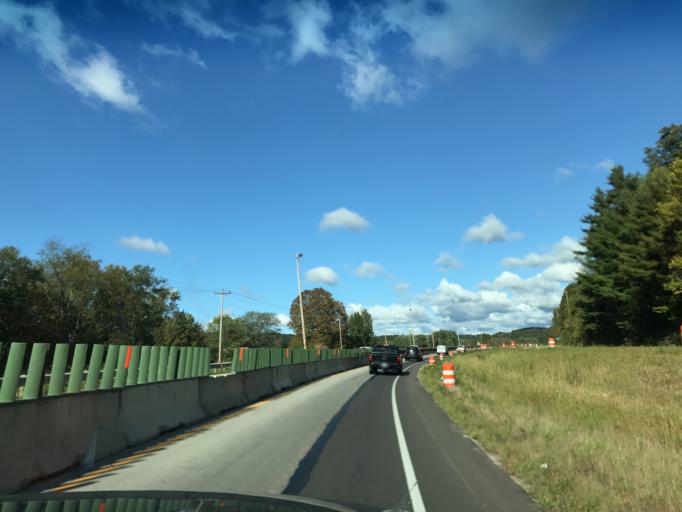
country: US
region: Ohio
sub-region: Athens County
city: Chauncey
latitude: 39.4057
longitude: -82.1783
